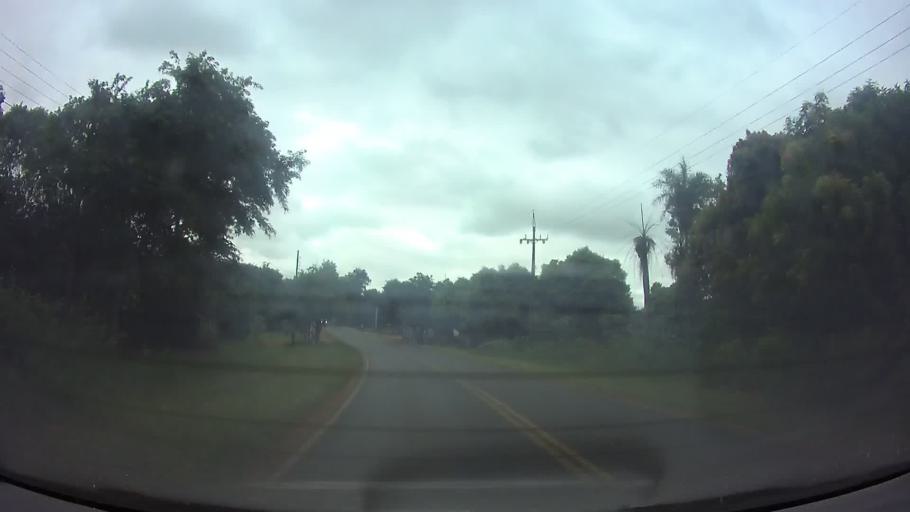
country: PY
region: Central
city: Nueva Italia
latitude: -25.5462
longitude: -57.4991
